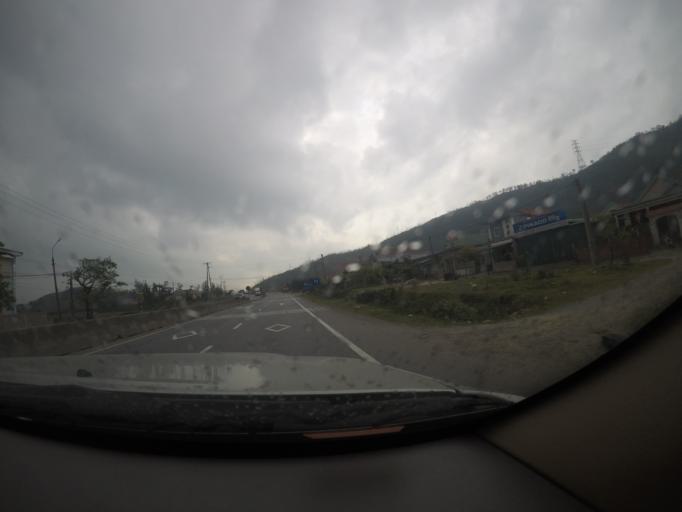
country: VN
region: Ha Tinh
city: Ky Anh
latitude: 17.9882
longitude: 106.4766
